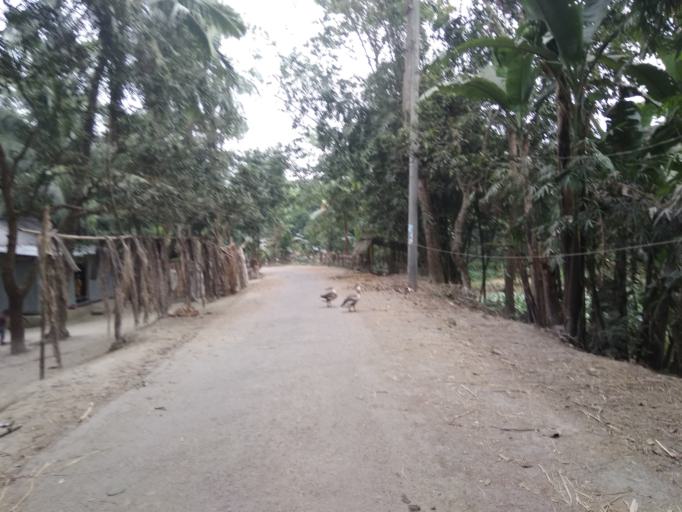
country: BD
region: Barisal
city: Mehendiganj
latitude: 22.9192
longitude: 90.3913
